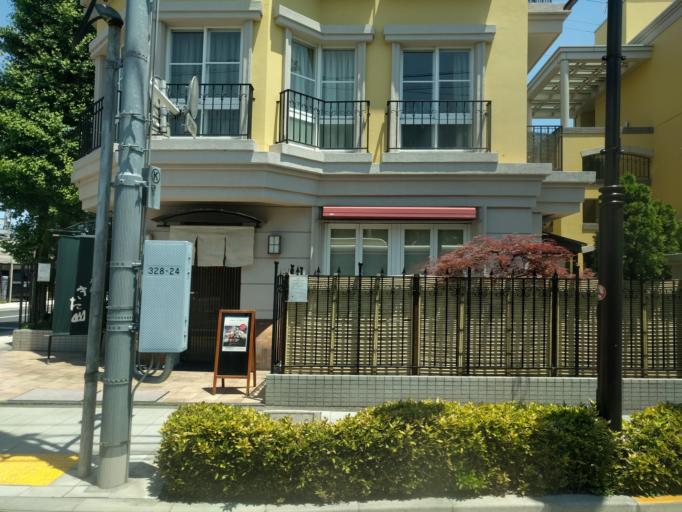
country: JP
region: Tokyo
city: Chofugaoka
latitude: 35.6415
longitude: 139.5966
